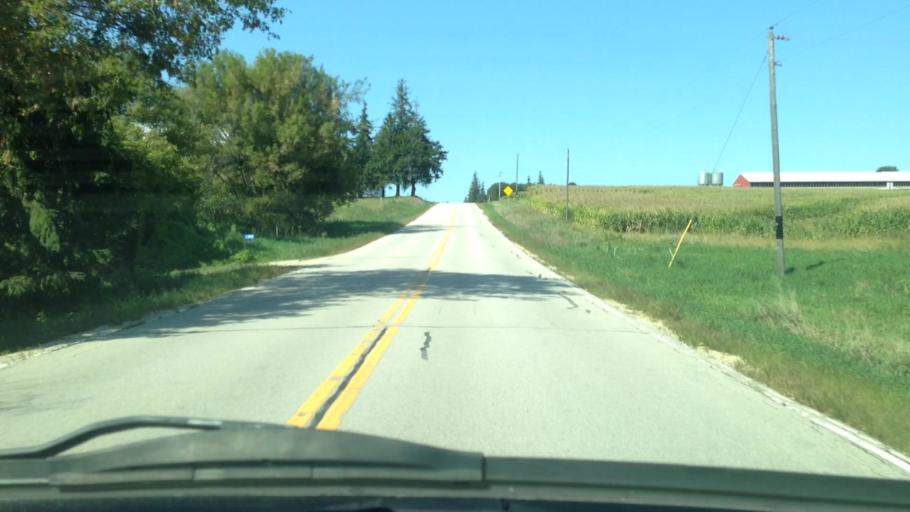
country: US
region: Minnesota
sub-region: Fillmore County
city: Rushford
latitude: 43.7021
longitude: -91.7704
